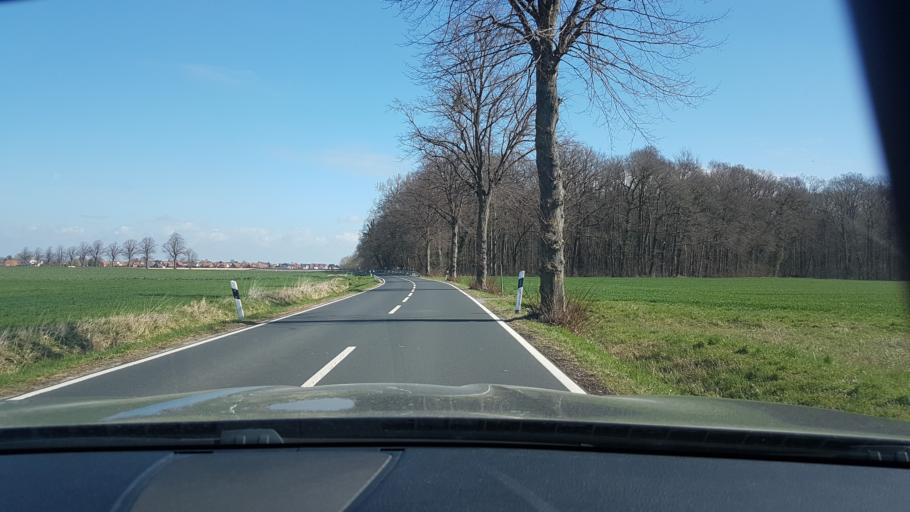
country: DE
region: Lower Saxony
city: Pattensen
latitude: 52.2298
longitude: 9.7233
